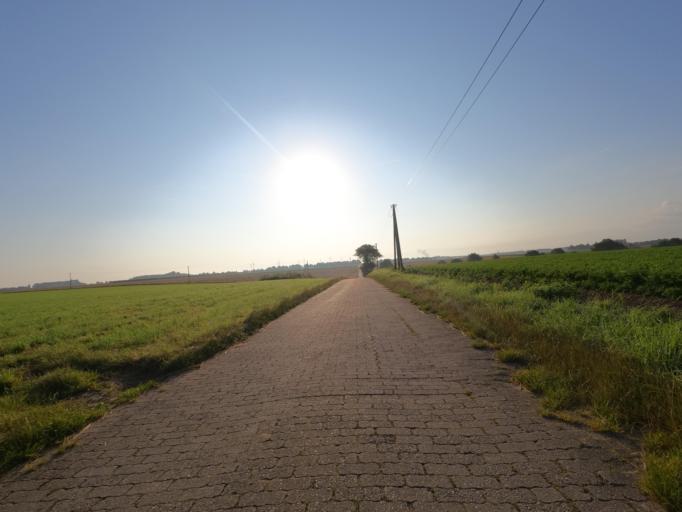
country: DE
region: North Rhine-Westphalia
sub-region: Regierungsbezirk Koln
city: Titz
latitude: 51.0173
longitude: 6.3708
